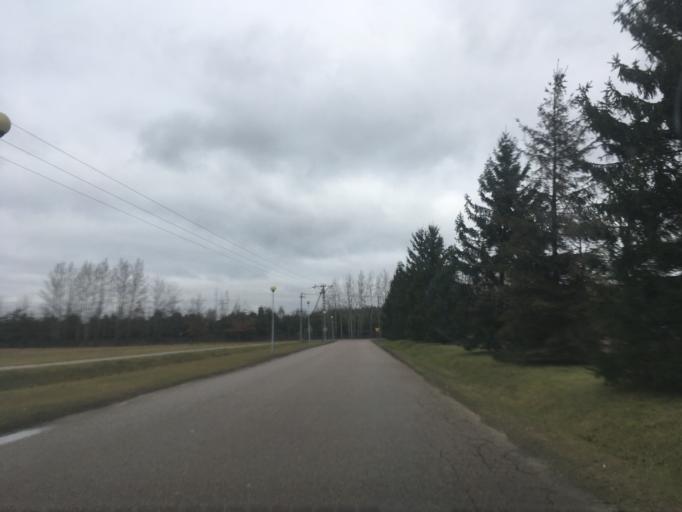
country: PL
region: Masovian Voivodeship
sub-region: Powiat piaseczynski
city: Lesznowola
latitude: 52.0596
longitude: 20.9071
